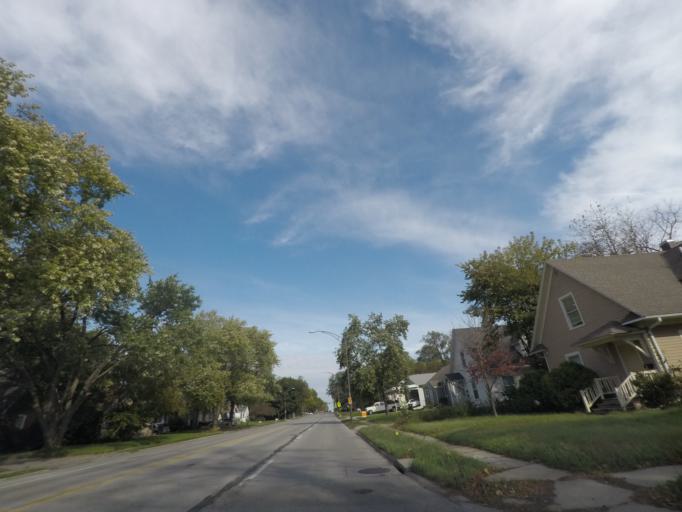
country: US
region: Iowa
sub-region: Story County
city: Ames
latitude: 42.0321
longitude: -93.6203
